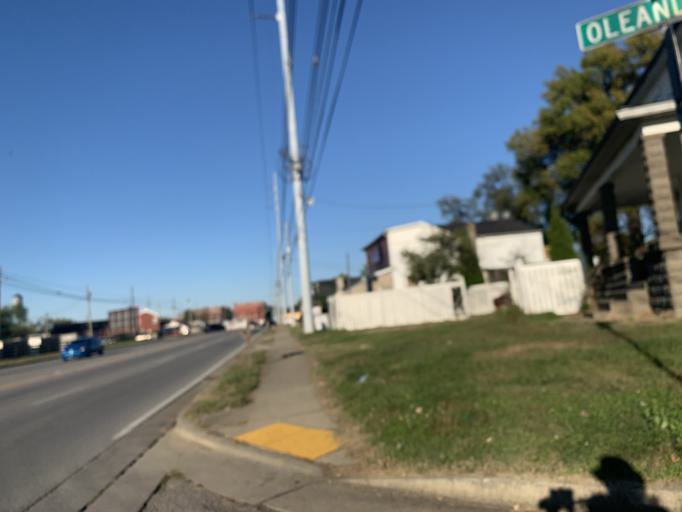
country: US
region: Kentucky
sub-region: Jefferson County
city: Shively
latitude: 38.2076
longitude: -85.7883
